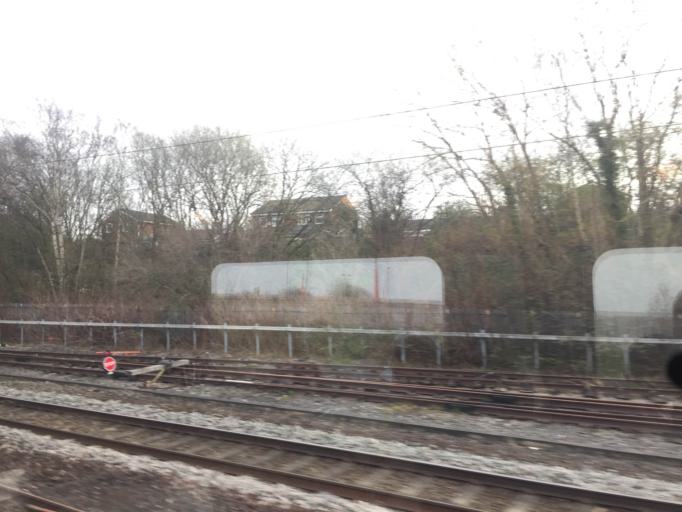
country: GB
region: England
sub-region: Warrington
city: Warrington
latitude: 53.3910
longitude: -2.6039
